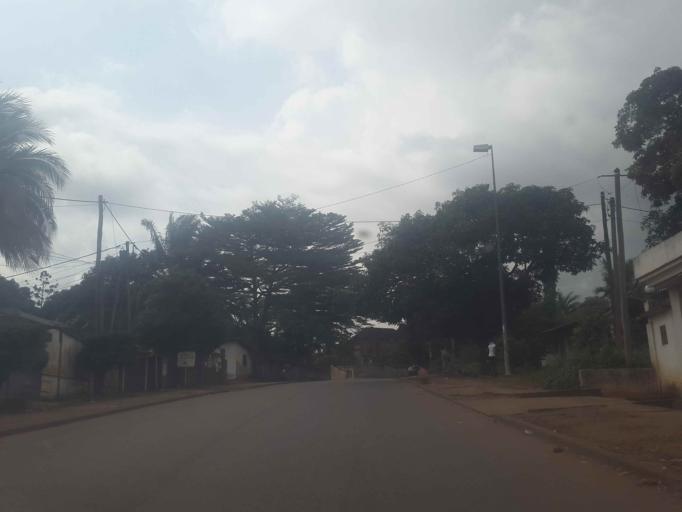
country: CM
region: Centre
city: Yaounde
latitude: 3.8730
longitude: 11.4845
